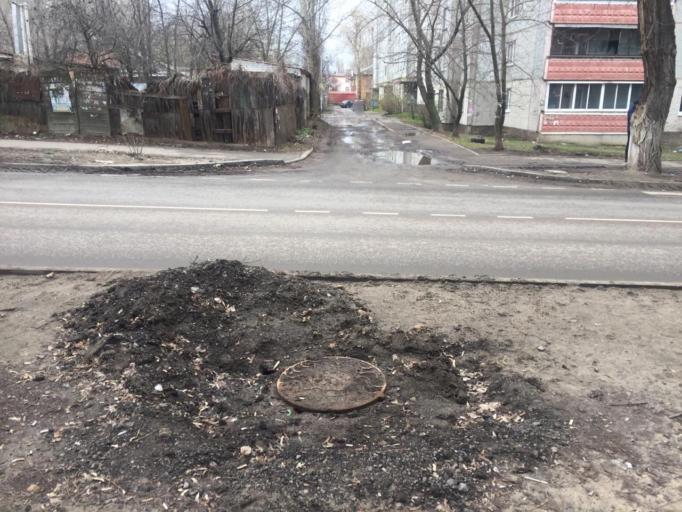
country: RU
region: Voronezj
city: Voronezh
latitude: 51.6745
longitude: 39.1513
